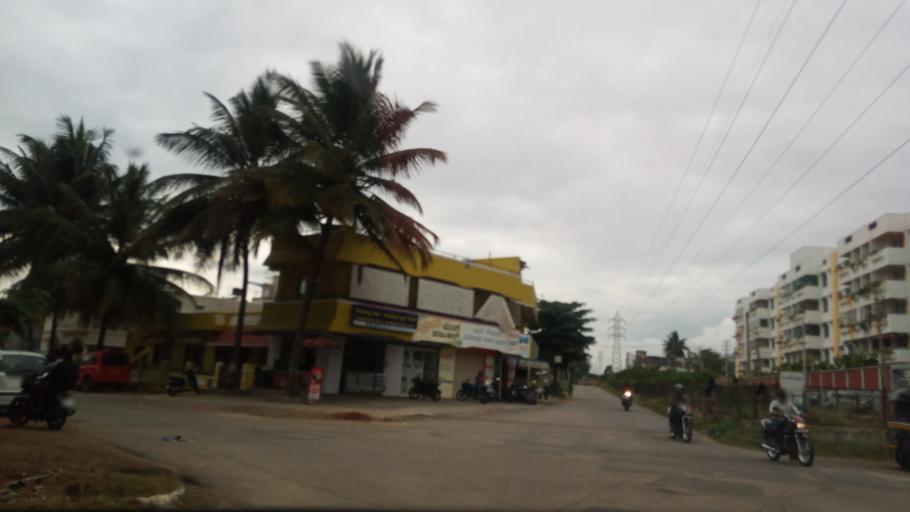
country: IN
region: Karnataka
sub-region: Mysore
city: Mysore
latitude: 12.2926
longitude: 76.6170
